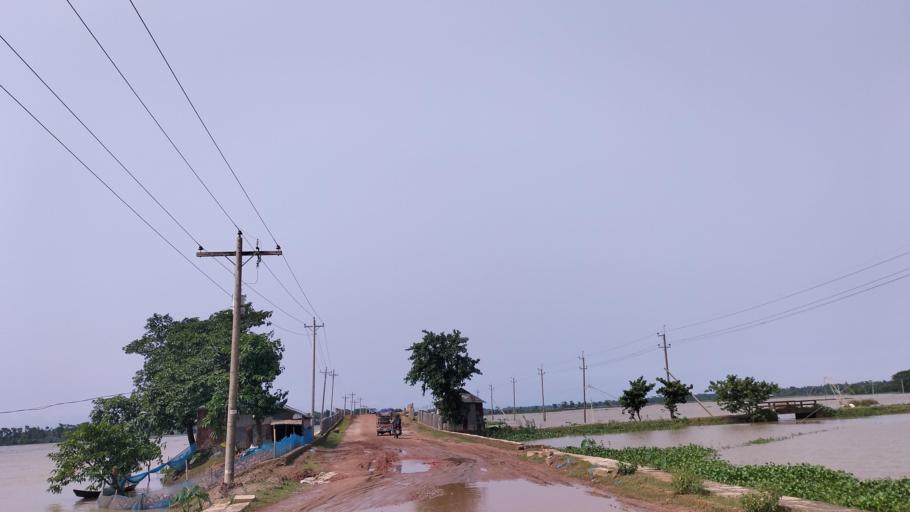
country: BD
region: Dhaka
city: Netrakona
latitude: 25.0194
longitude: 90.8577
